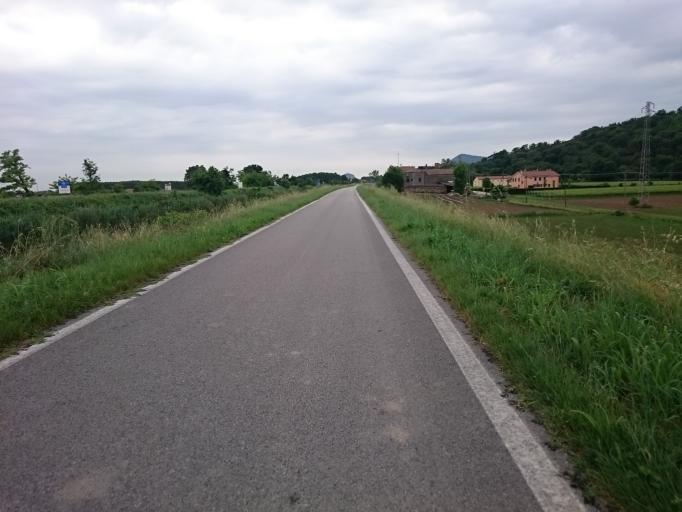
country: IT
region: Veneto
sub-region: Provincia di Padova
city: Battaglia Terme
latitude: 45.3042
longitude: 11.7952
